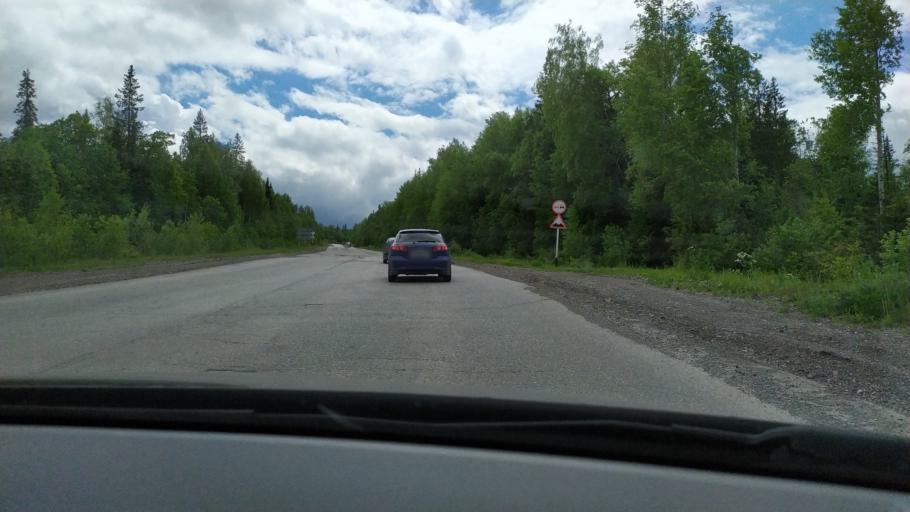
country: RU
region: Perm
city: Gremyachinsk
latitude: 58.4387
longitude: 57.8841
